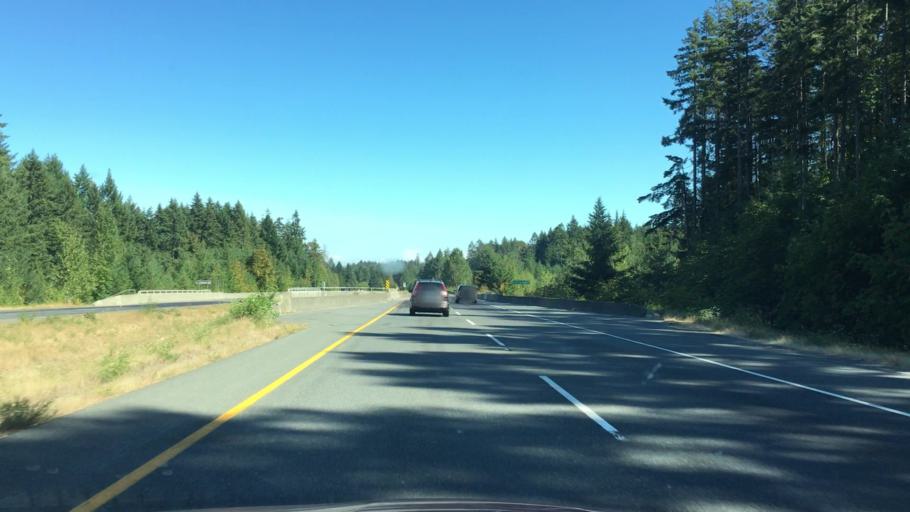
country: CA
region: British Columbia
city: Nanaimo
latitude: 49.1425
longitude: -123.9666
